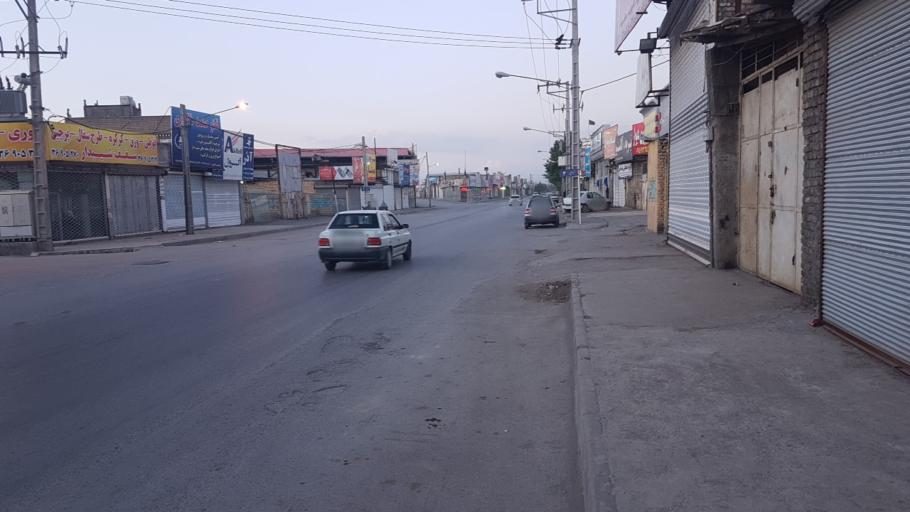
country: IR
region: Razavi Khorasan
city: Mashhad
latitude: 36.3510
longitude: 59.5787
